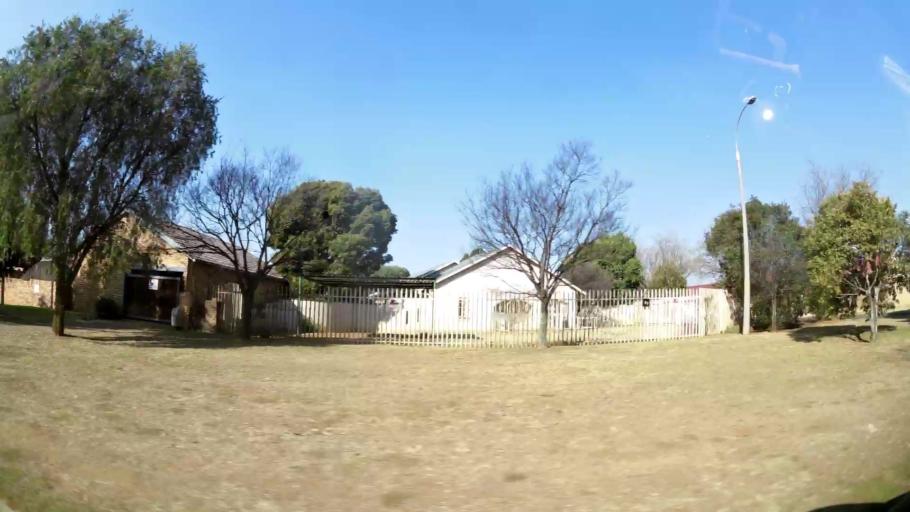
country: ZA
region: Gauteng
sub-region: West Rand District Municipality
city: Randfontein
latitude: -26.1764
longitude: 27.6882
